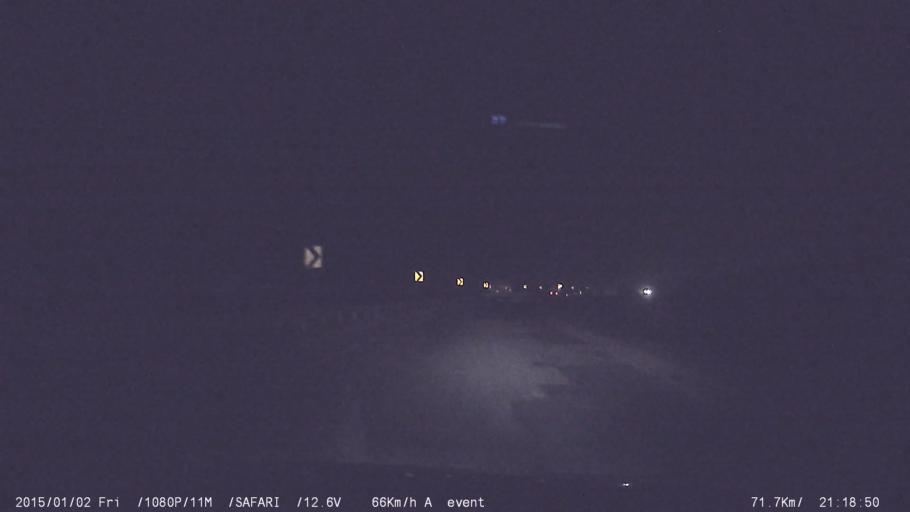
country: IN
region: Tamil Nadu
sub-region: Kancheepuram
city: Kanchipuram
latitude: 12.8740
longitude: 79.6181
